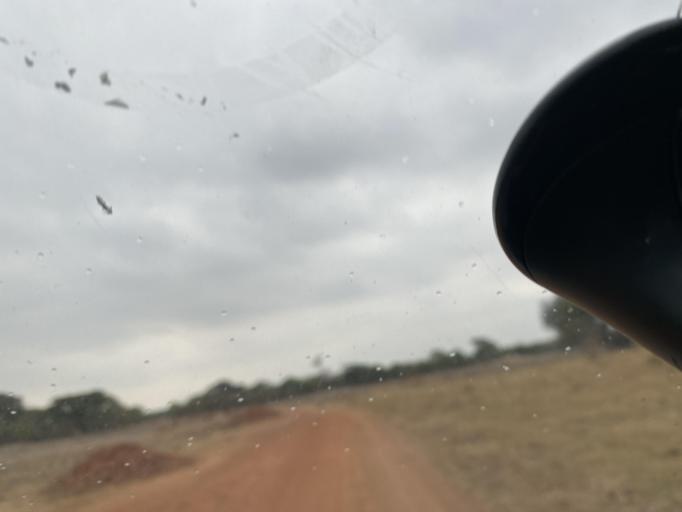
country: ZM
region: Lusaka
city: Chongwe
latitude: -15.1562
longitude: 28.7463
